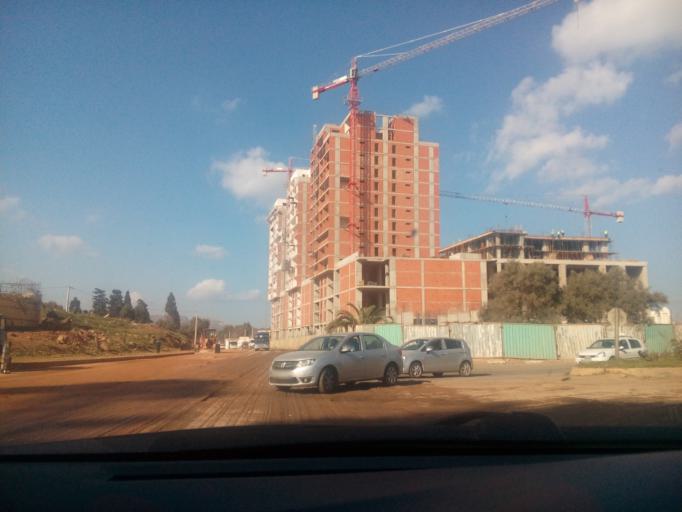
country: DZ
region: Oran
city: Es Senia
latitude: 35.6792
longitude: -0.6050
